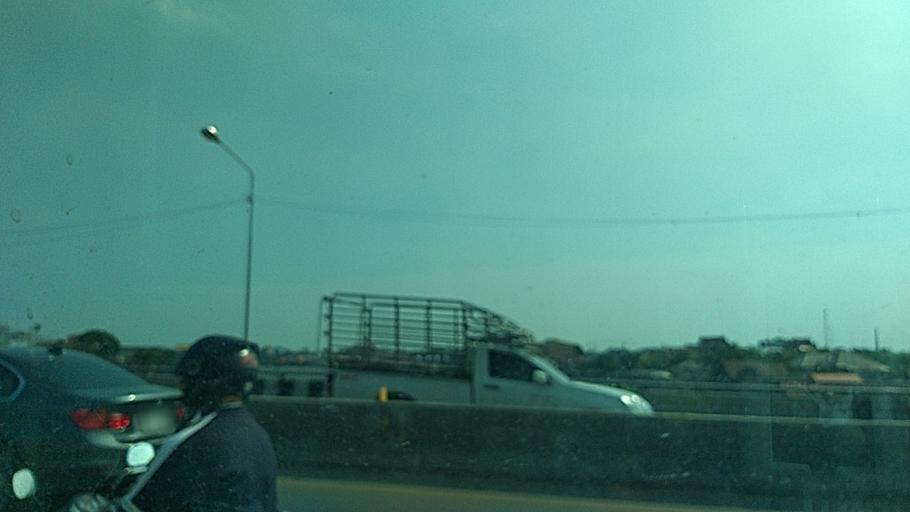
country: TH
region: Pathum Thani
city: Pathum Thani
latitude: 14.0265
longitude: 100.5385
